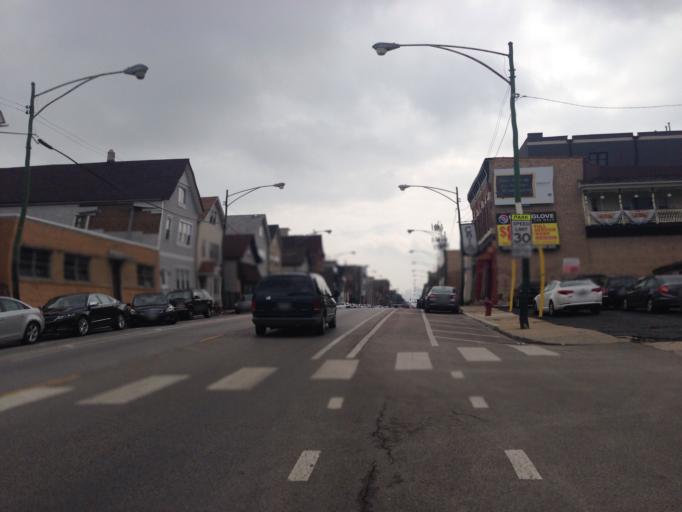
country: US
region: Illinois
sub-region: Cook County
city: Chicago
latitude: 41.9274
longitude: -87.6726
